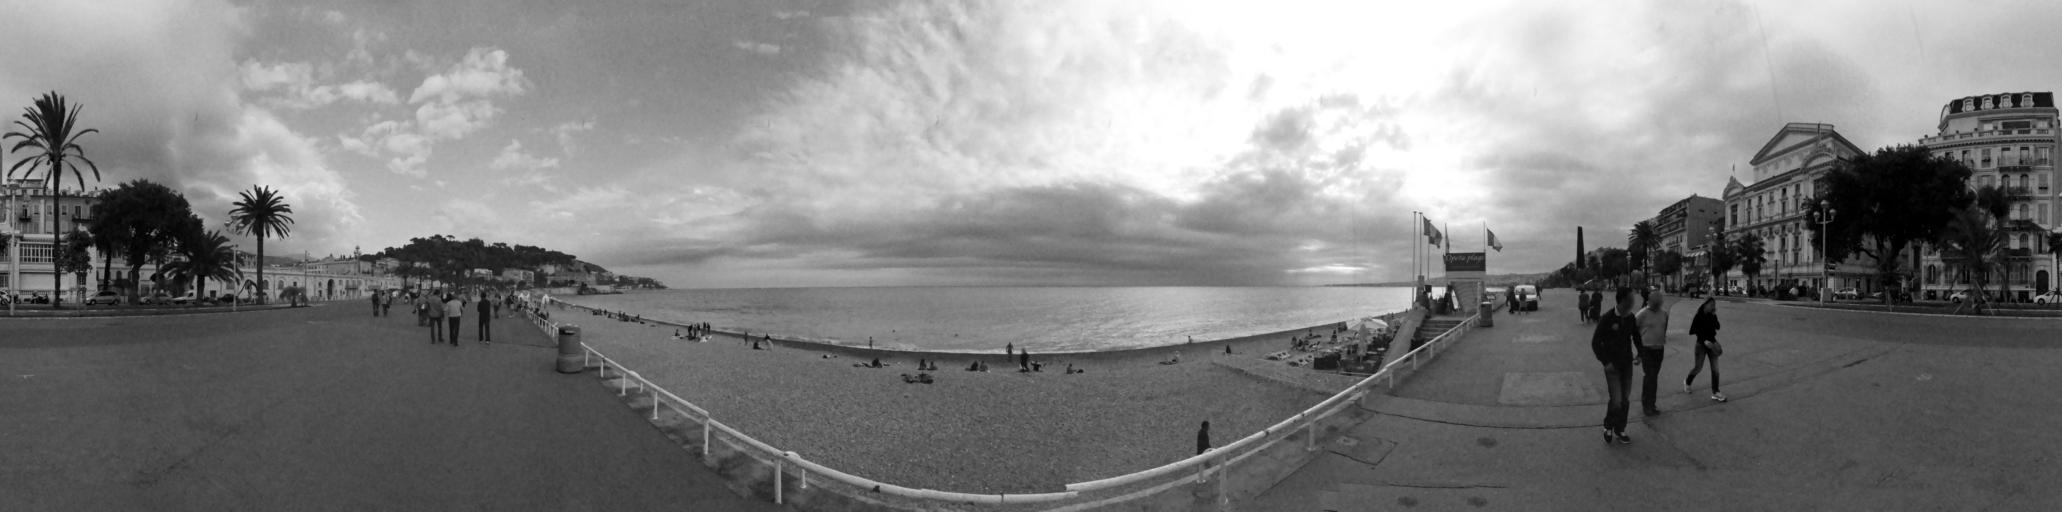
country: FR
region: Provence-Alpes-Cote d'Azur
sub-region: Departement des Alpes-Maritimes
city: Nice
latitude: 43.6949
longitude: 7.2731
